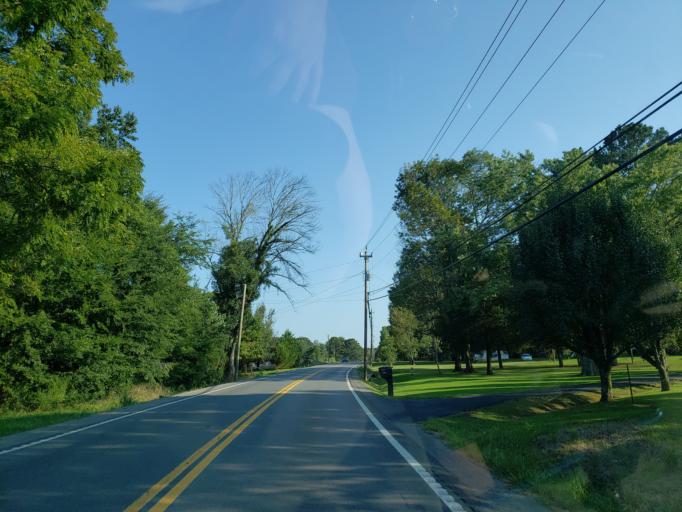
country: US
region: Tennessee
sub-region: Bradley County
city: Wildwood Lake
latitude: 35.0768
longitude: -84.8160
